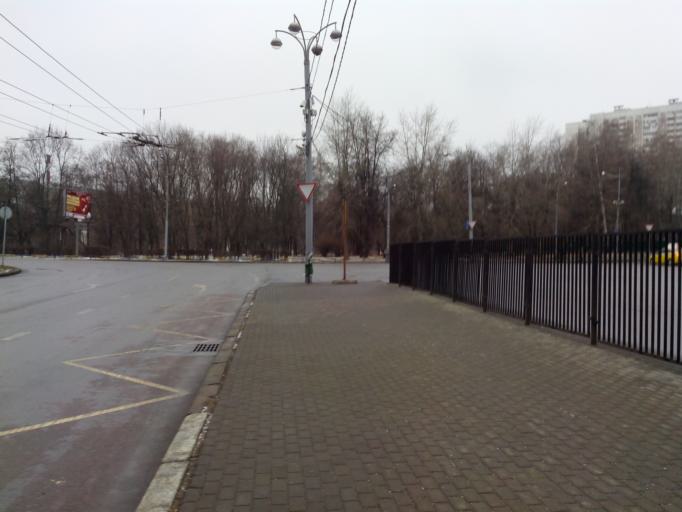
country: RU
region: Moscow
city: Ostankinskiy
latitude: 55.8235
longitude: 37.6351
